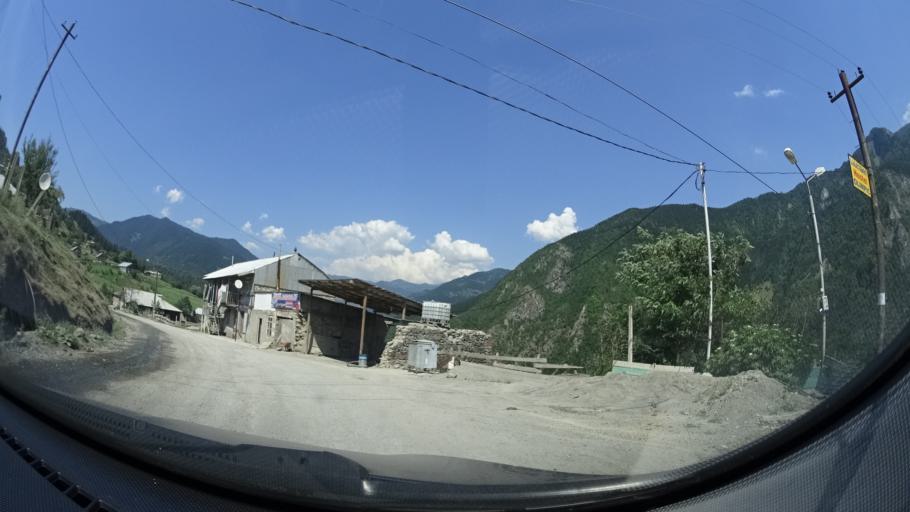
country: GE
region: Ajaria
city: Khulo
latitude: 41.6449
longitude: 42.3187
